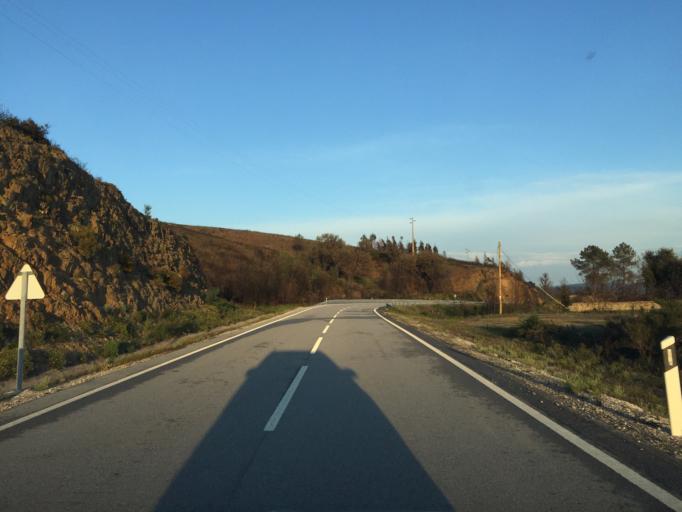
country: PT
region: Coimbra
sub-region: Pampilhosa da Serra
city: Pampilhosa da Serra
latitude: 40.0838
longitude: -7.9902
